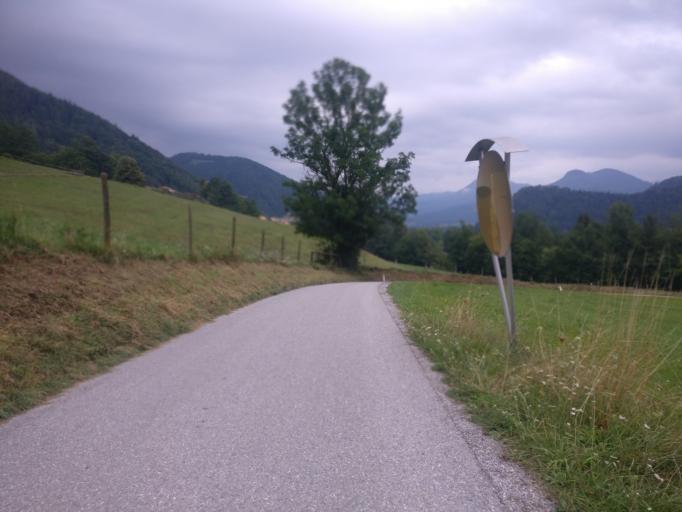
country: AT
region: Styria
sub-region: Politischer Bezirk Graz-Umgebung
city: Frohnleiten
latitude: 47.2343
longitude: 15.3120
